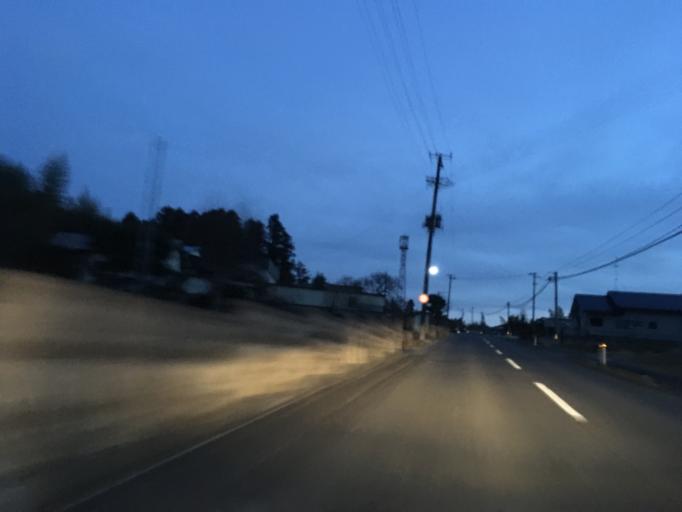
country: JP
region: Miyagi
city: Wakuya
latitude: 38.6959
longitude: 141.1636
